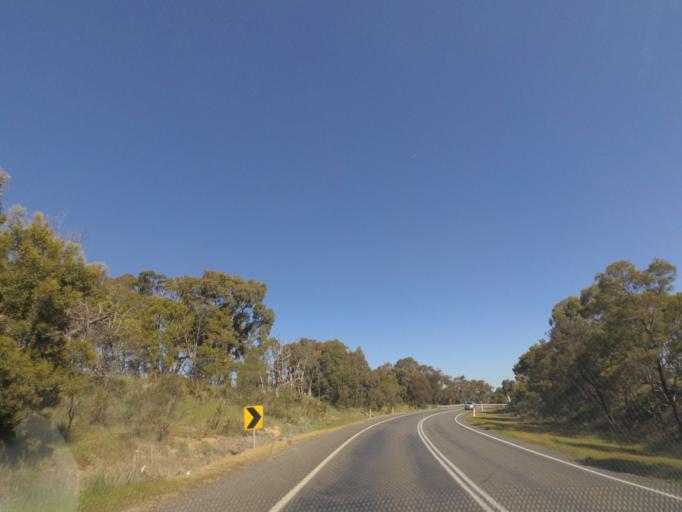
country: AU
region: Victoria
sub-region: Whittlesea
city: Whittlesea
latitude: -37.3290
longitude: 144.9835
